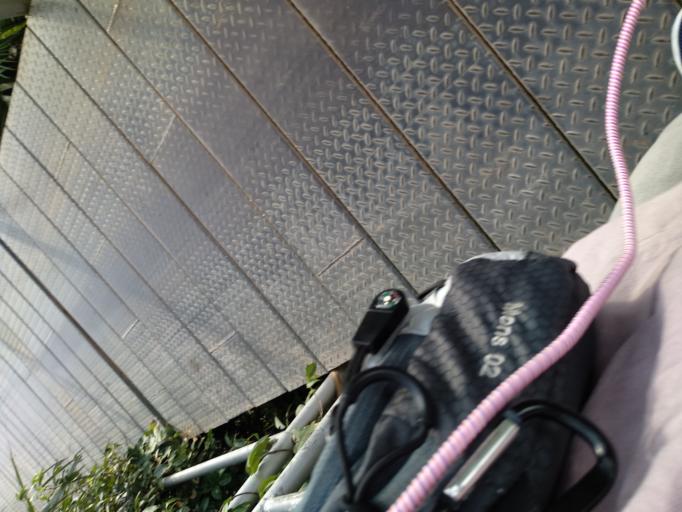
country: ID
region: South Kalimantan
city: Aluhaluh
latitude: -3.4717
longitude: 114.5305
